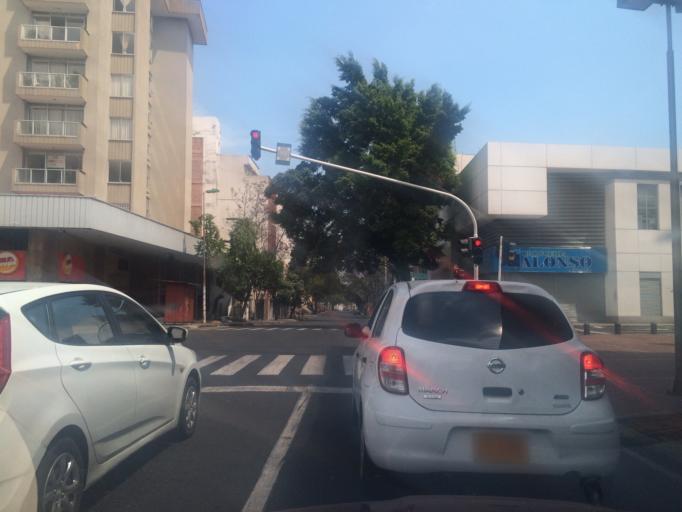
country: CO
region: Valle del Cauca
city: Cali
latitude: 3.4503
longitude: -76.5351
